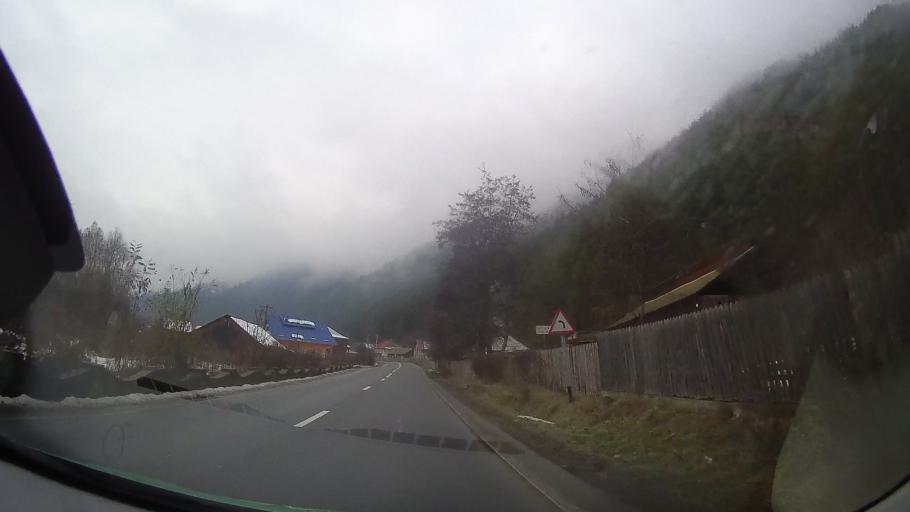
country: RO
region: Neamt
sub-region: Comuna Bicaz Chei
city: Bicaz Chei
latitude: 46.8422
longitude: 25.8984
